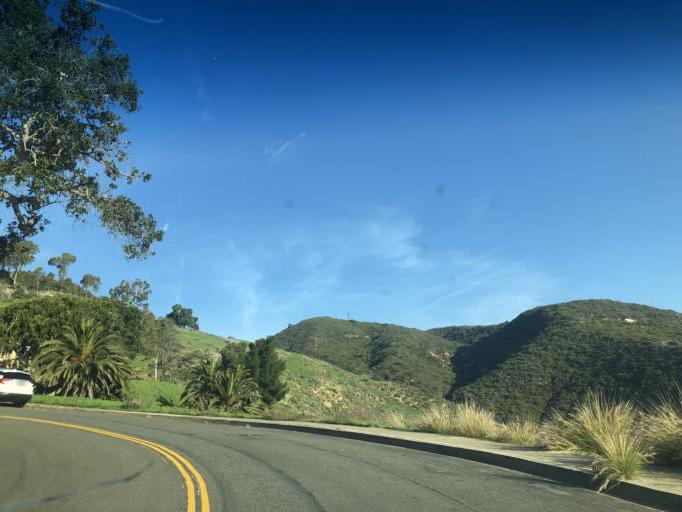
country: US
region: California
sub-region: Orange County
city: Laguna Beach
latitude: 33.5486
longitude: -117.7845
